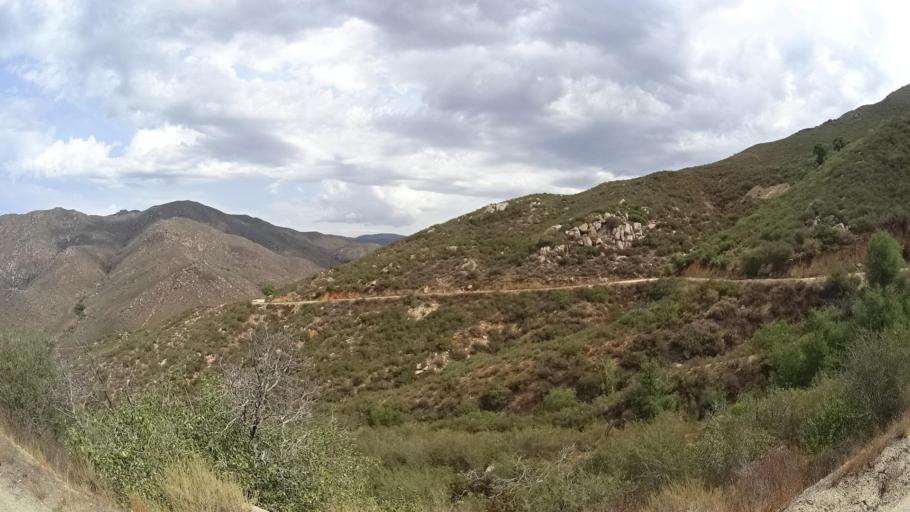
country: US
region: California
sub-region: San Diego County
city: Ramona
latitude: 33.1168
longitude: -116.8127
